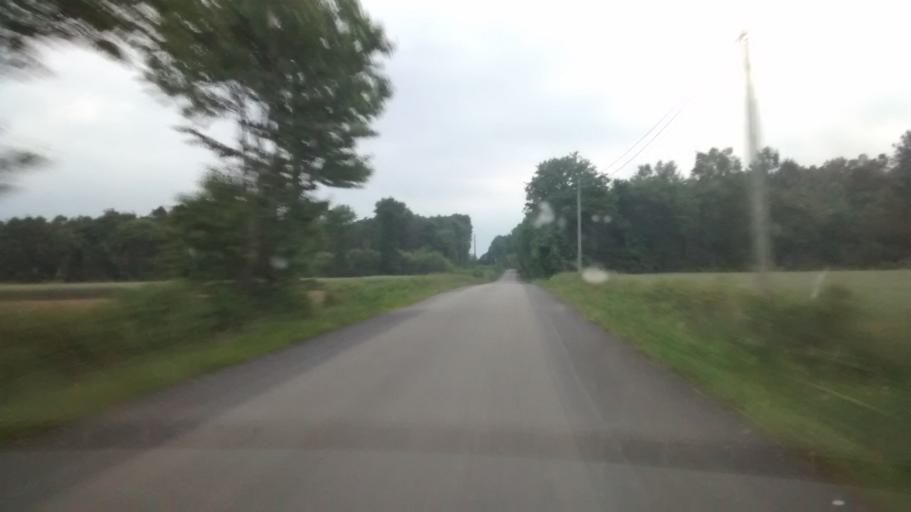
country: FR
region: Brittany
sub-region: Departement du Morbihan
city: Malansac
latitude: 47.7321
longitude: -2.3135
